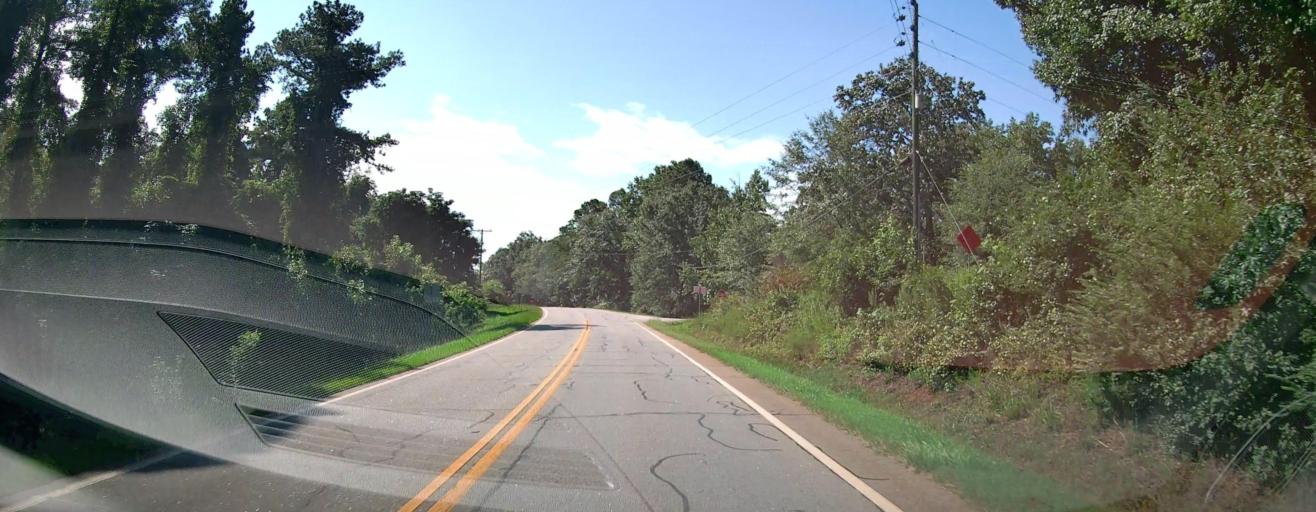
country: US
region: Georgia
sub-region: Upson County
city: Thomaston
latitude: 32.9007
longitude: -84.3544
